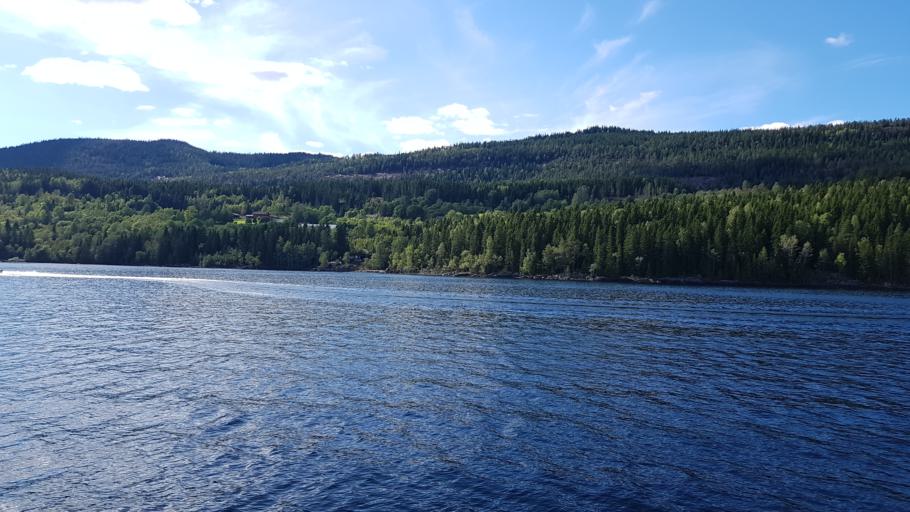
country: NO
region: Akershus
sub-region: Hurdal
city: Hurdal
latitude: 60.5411
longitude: 11.1990
